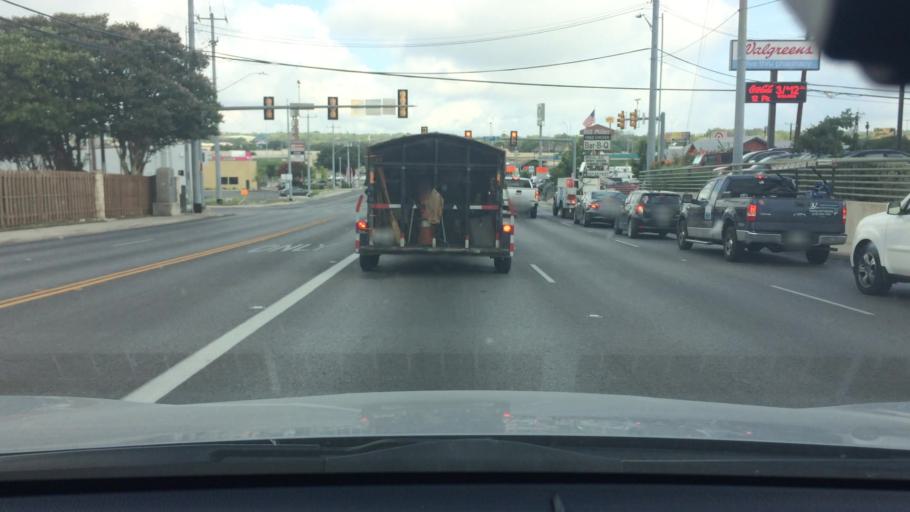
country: US
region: Texas
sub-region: Bexar County
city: Hollywood Park
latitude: 29.5629
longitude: -98.4799
